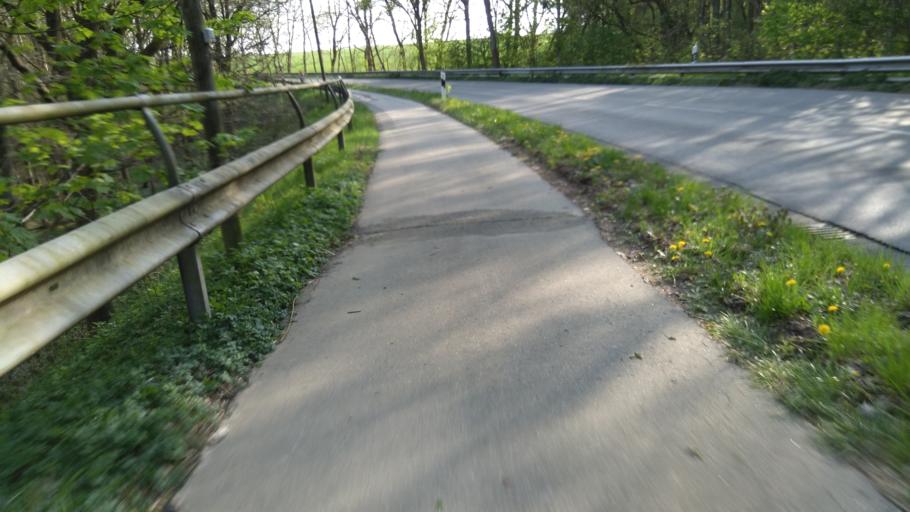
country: DE
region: Lower Saxony
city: Buxtehude
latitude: 53.4383
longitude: 9.6579
